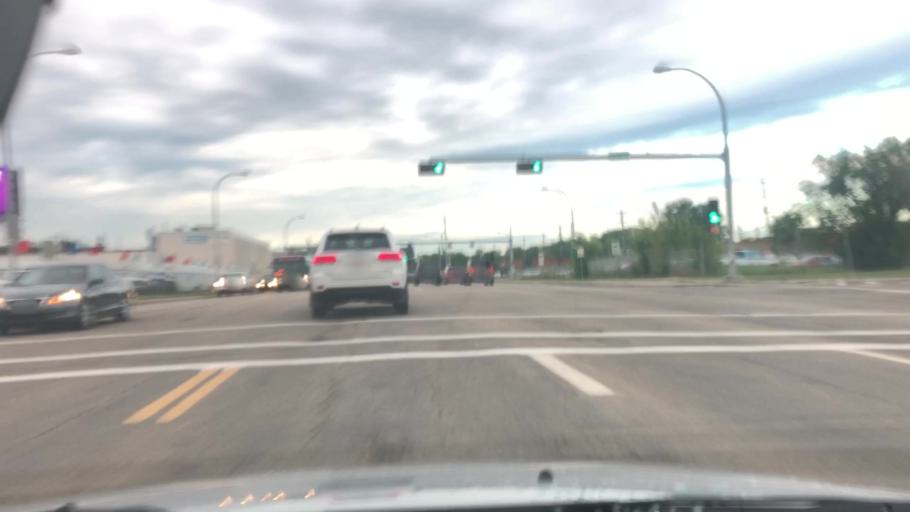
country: CA
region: Alberta
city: Edmonton
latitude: 53.5825
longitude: -113.5412
